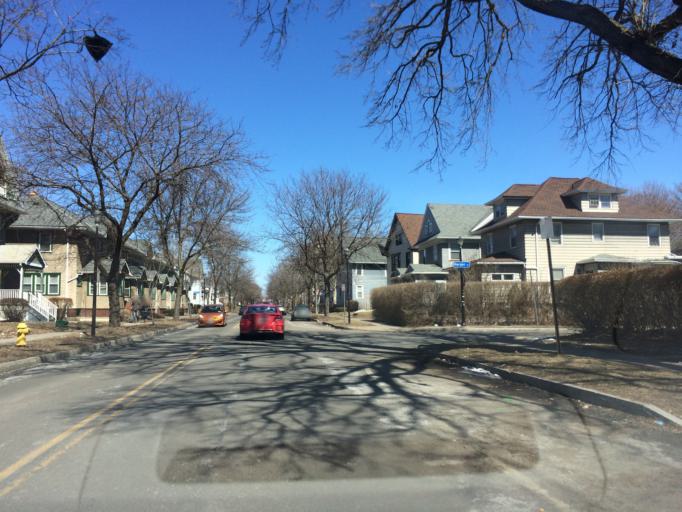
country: US
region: New York
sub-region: Monroe County
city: Rochester
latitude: 43.1469
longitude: -77.5919
